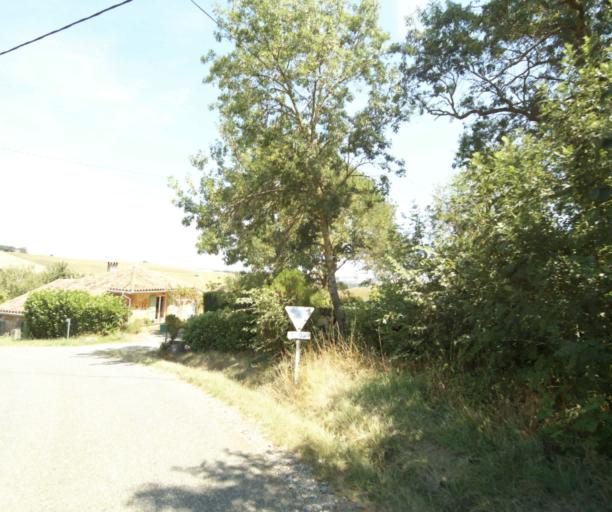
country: FR
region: Midi-Pyrenees
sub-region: Departement de l'Ariege
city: Lezat-sur-Leze
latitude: 43.2702
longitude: 1.3094
